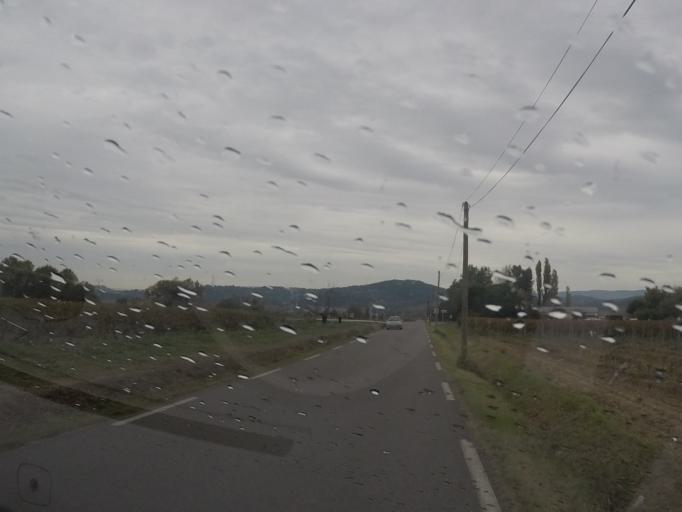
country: FR
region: Provence-Alpes-Cote d'Azur
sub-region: Departement du Vaucluse
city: Bonnieux
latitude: 43.8458
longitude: 5.2857
